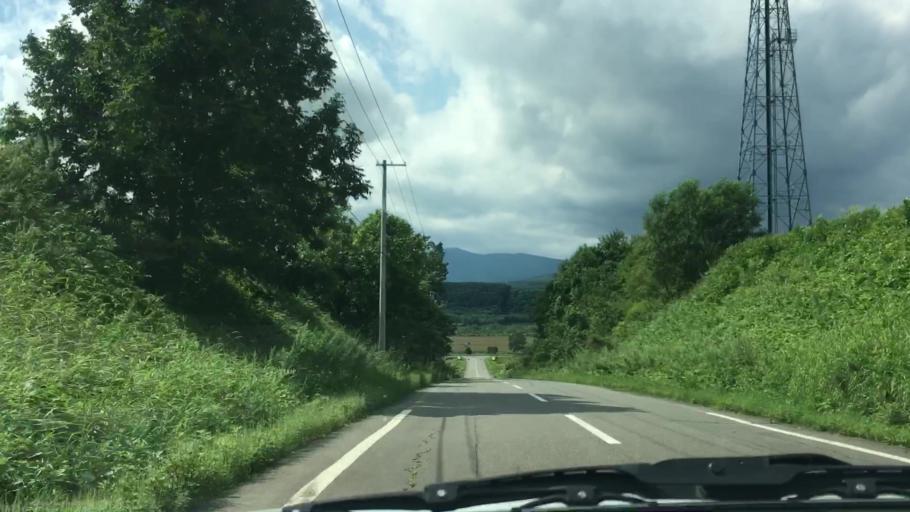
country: JP
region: Hokkaido
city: Otofuke
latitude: 43.2837
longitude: 143.3111
